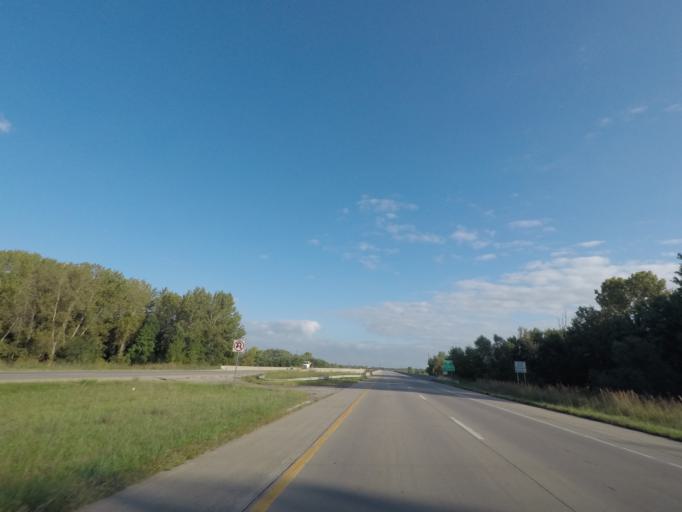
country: US
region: Iowa
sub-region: Polk County
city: Pleasant Hill
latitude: 41.5629
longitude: -93.5111
